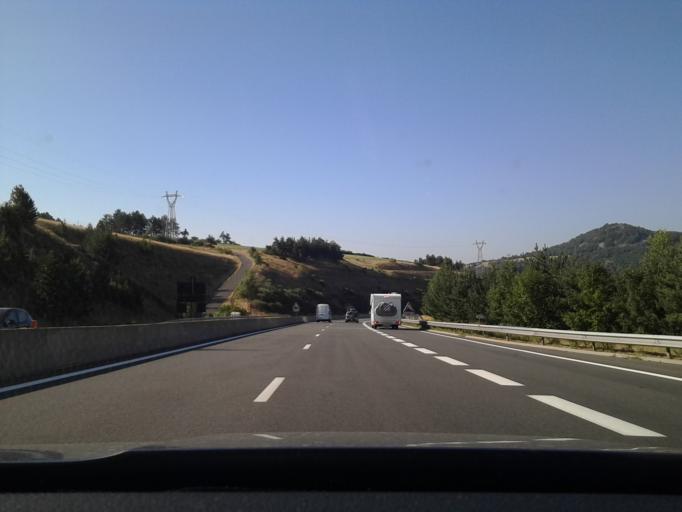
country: FR
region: Languedoc-Roussillon
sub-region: Departement de la Lozere
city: Chirac
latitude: 44.5433
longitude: 3.2571
